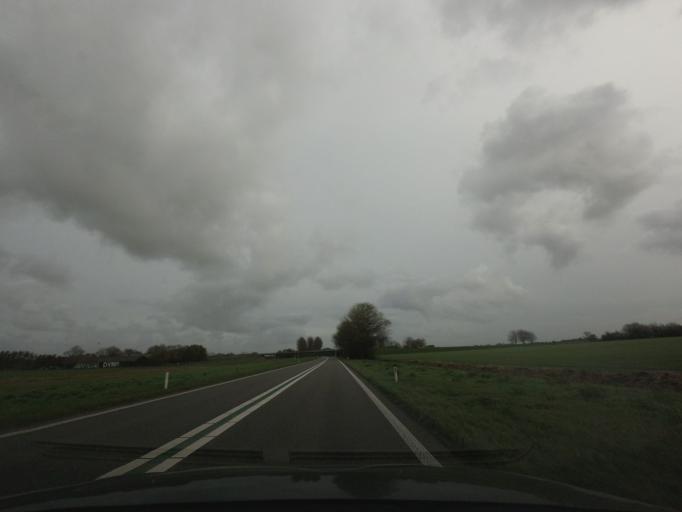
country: NL
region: North Holland
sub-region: Gemeente Opmeer
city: Opmeer
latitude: 52.7290
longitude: 4.8885
